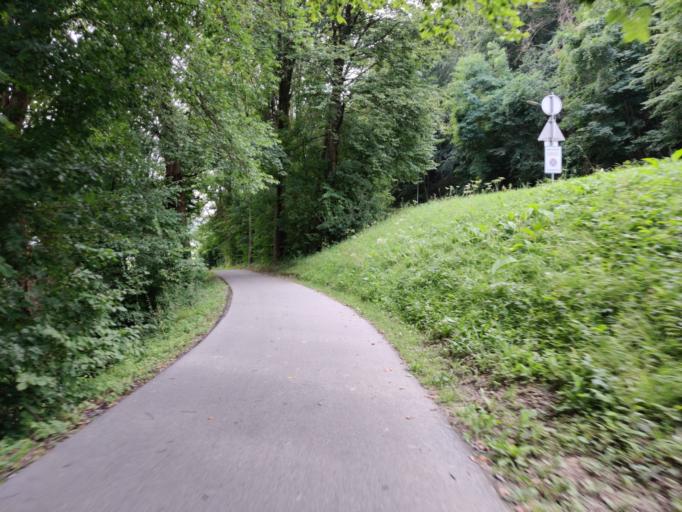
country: AT
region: Lower Austria
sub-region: Politischer Bezirk Melk
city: Ybbs an der Donau
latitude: 48.1869
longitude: 15.0693
